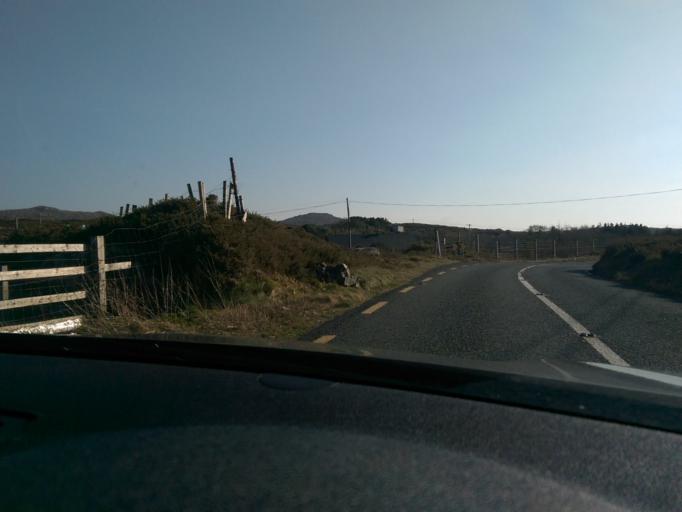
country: IE
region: Connaught
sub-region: County Galway
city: Clifden
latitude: 53.3913
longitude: -9.7769
